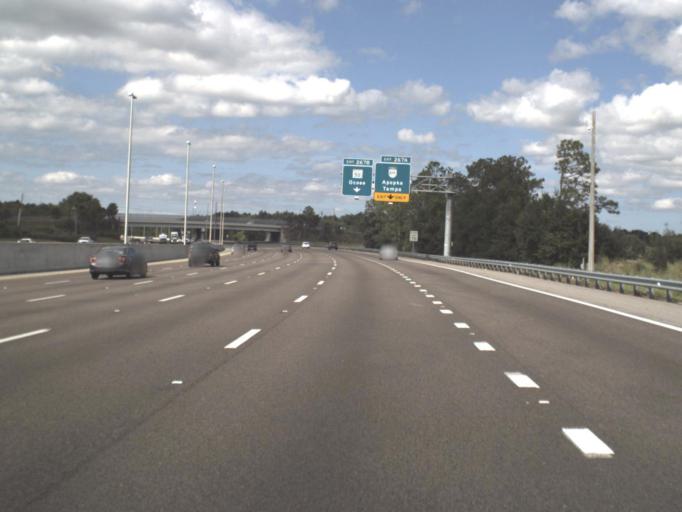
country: US
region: Florida
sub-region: Orange County
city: Gotha
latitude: 28.5443
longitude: -81.5384
